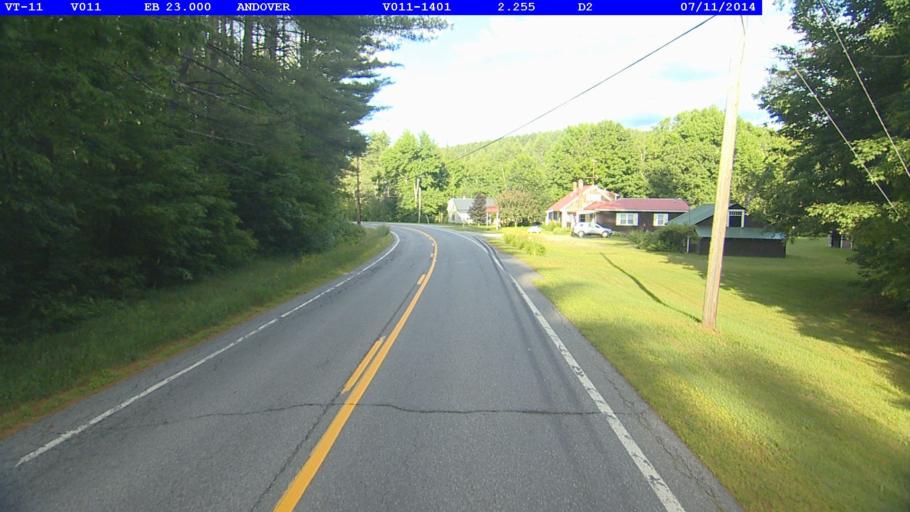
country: US
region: Vermont
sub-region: Windsor County
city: Chester
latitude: 43.2585
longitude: -72.7087
